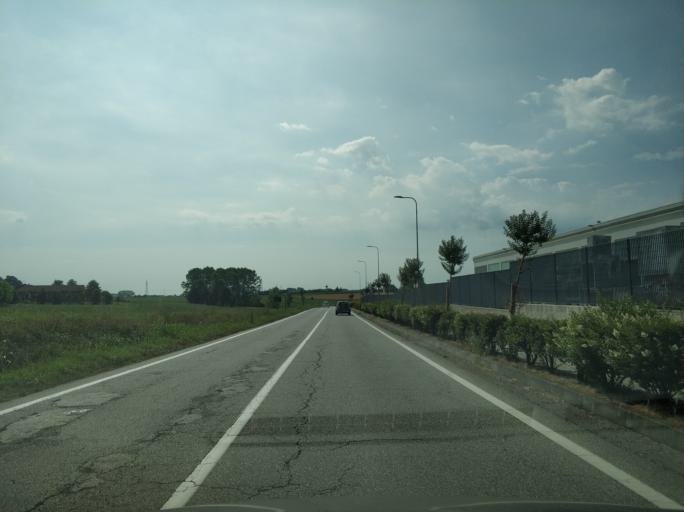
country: IT
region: Piedmont
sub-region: Provincia di Torino
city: Marocchi
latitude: 44.9382
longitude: 7.8244
